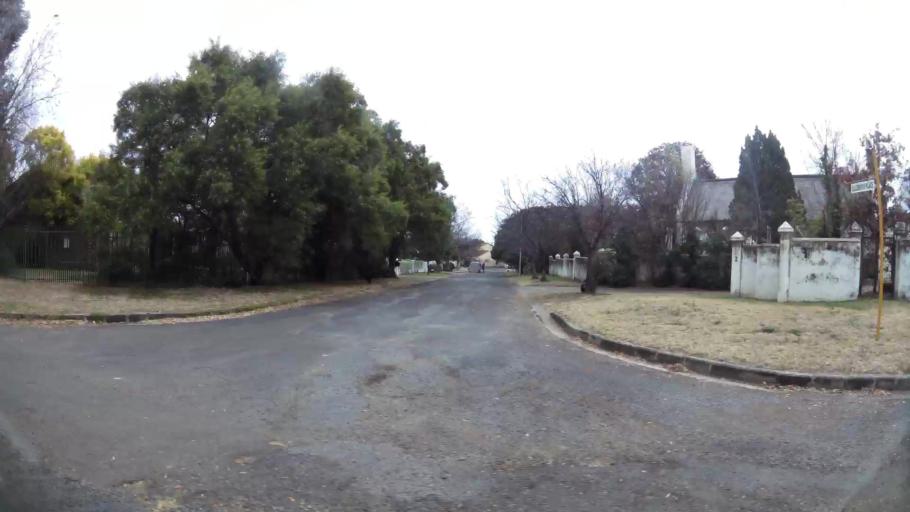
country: ZA
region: Orange Free State
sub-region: Fezile Dabi District Municipality
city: Kroonstad
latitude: -27.6761
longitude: 27.2484
